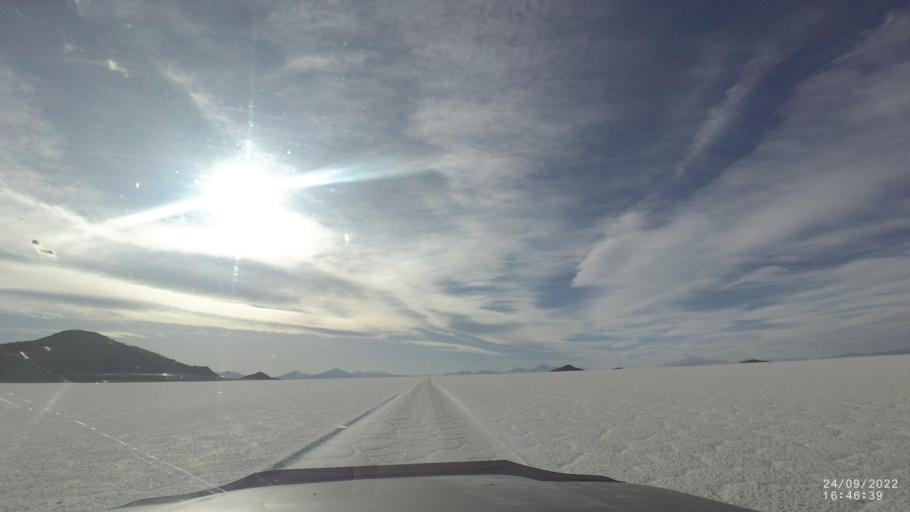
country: BO
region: Potosi
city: Colchani
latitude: -20.1360
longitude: -67.7933
